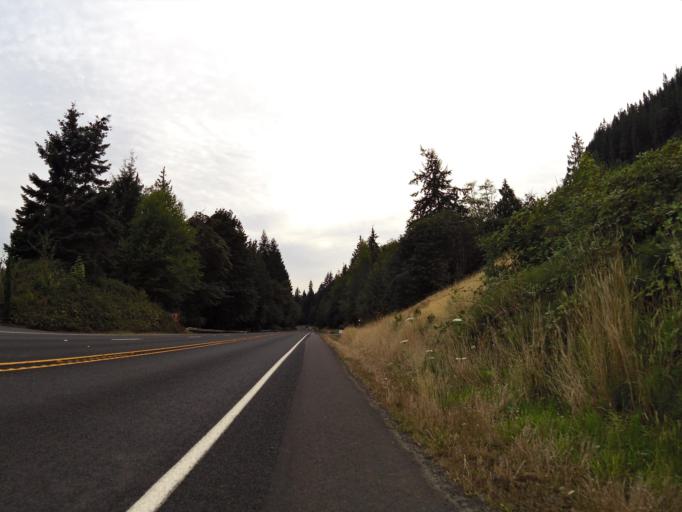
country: US
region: Oregon
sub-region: Columbia County
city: Clatskanie
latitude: 46.1608
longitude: -123.2547
